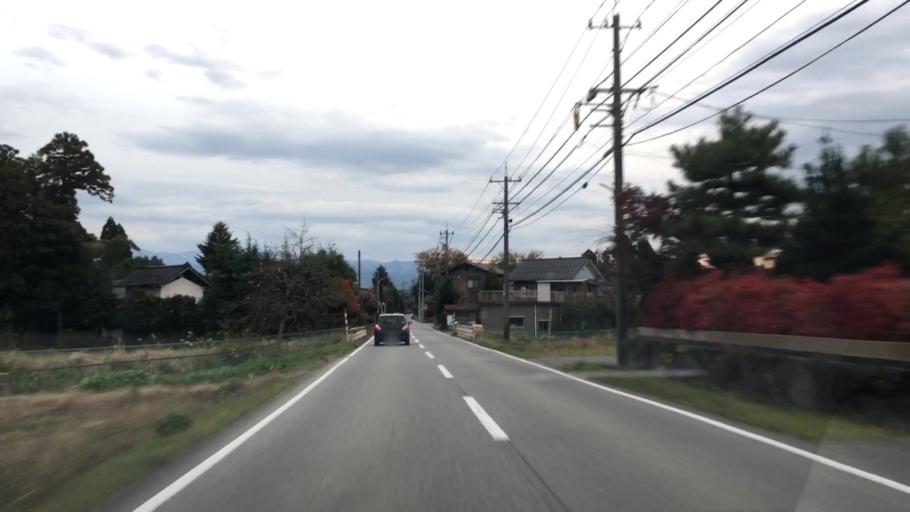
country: JP
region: Toyama
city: Kamiichi
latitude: 36.6951
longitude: 137.3151
